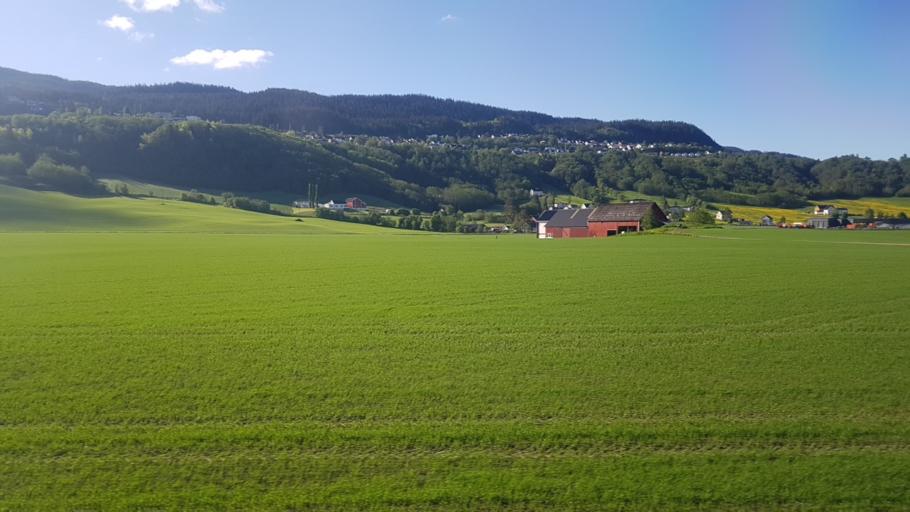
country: NO
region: Sor-Trondelag
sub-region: Melhus
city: Melhus
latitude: 63.3139
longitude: 10.3049
